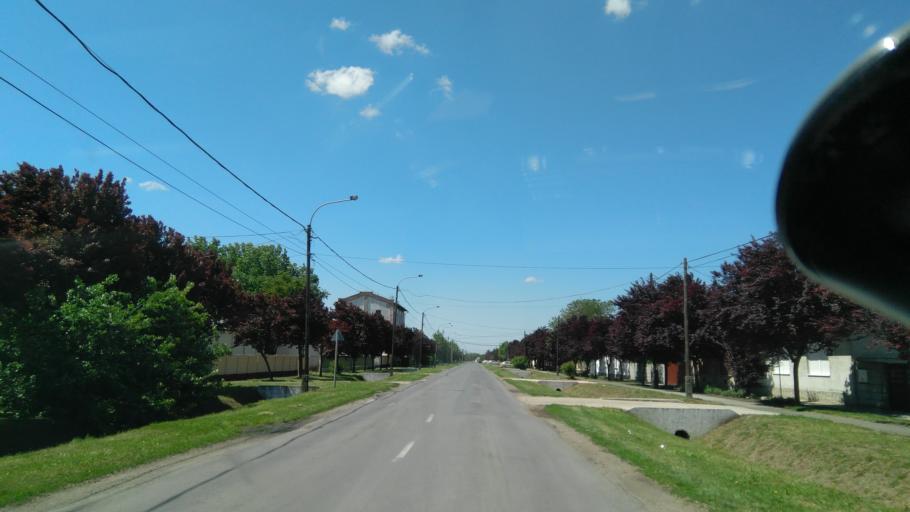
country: HU
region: Bekes
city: Kunagota
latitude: 46.4227
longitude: 21.0446
